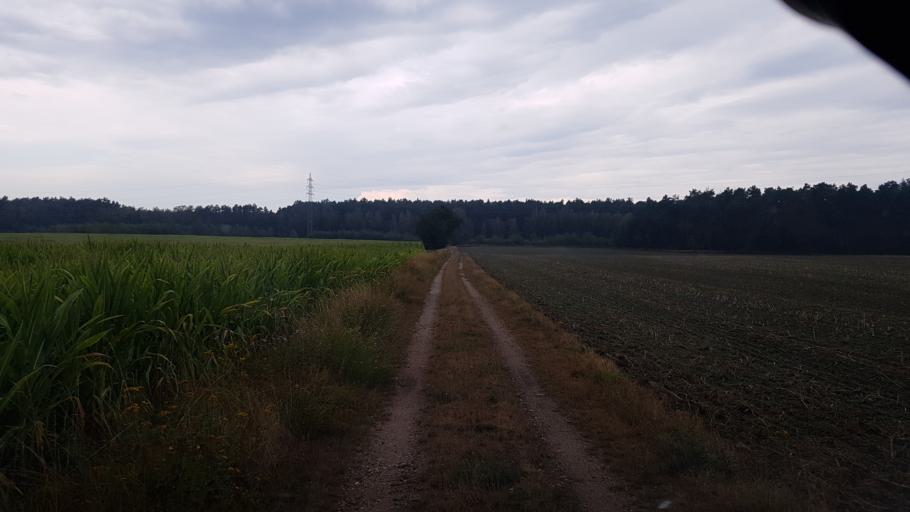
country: DE
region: Brandenburg
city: Finsterwalde
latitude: 51.6358
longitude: 13.7618
